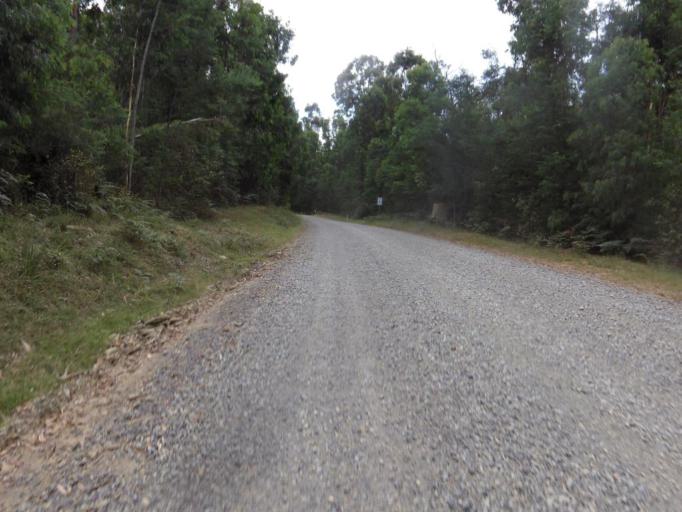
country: AU
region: Victoria
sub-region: Yarra Ranges
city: Healesville
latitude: -37.4171
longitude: 145.5650
